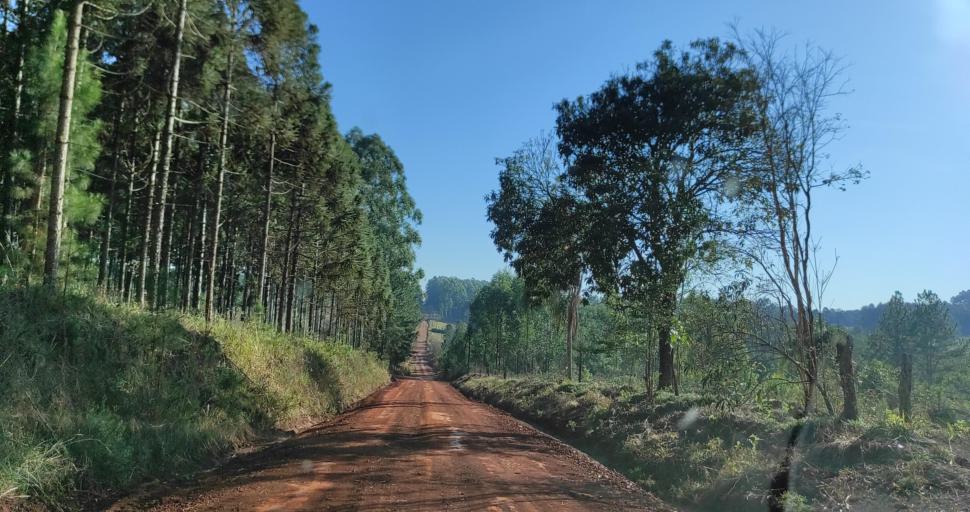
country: AR
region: Misiones
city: Capiovi
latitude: -26.8719
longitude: -55.0158
